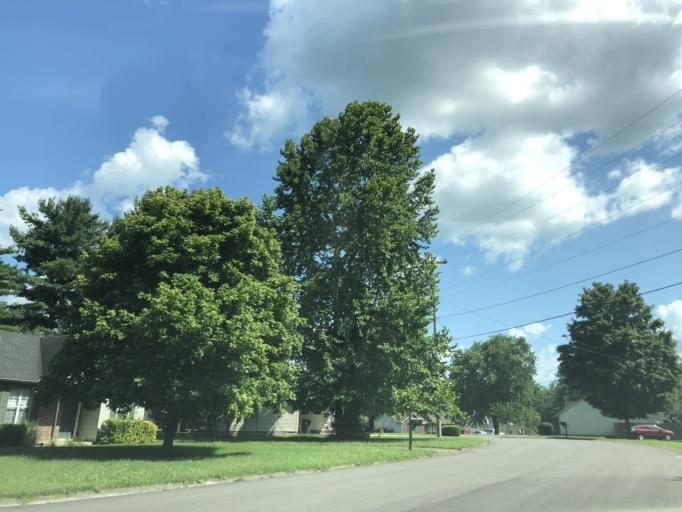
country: US
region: Tennessee
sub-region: Wilson County
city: Green Hill
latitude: 36.2049
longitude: -86.5883
